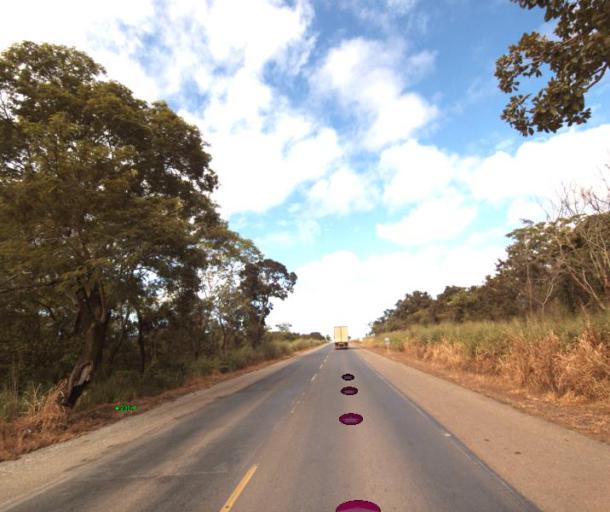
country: BR
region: Goias
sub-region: Uruacu
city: Uruacu
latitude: -14.7775
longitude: -49.2704
